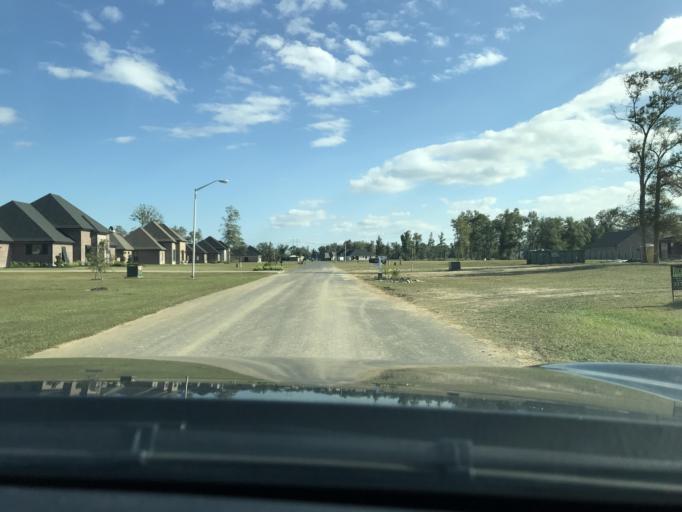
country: US
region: Louisiana
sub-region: Calcasieu Parish
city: Moss Bluff
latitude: 30.3361
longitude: -93.2513
